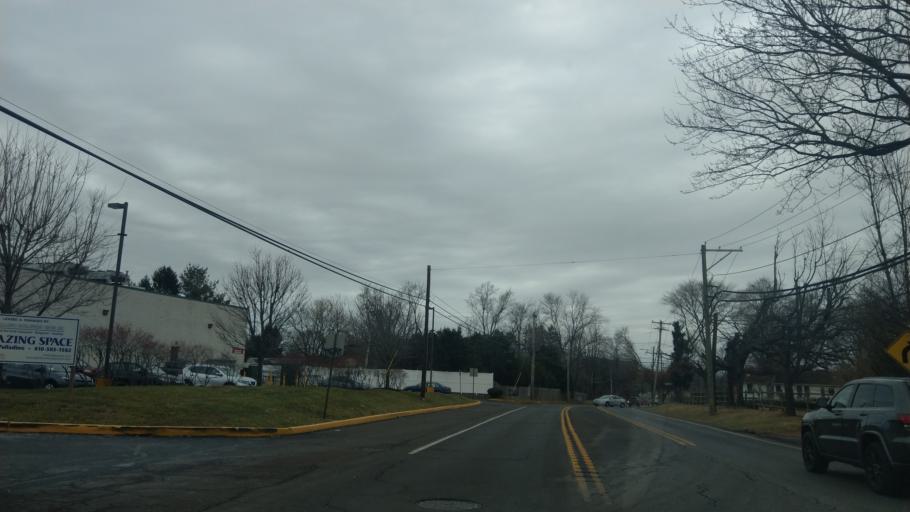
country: US
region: Pennsylvania
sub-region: Bucks County
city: Hulmeville
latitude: 40.1309
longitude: -74.9221
